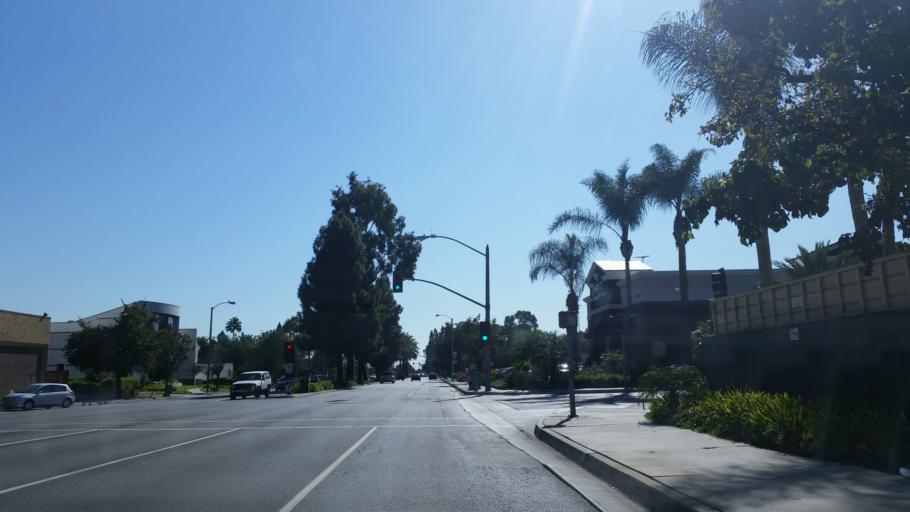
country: US
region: California
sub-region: Los Angeles County
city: Artesia
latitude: 33.8617
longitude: -118.0910
